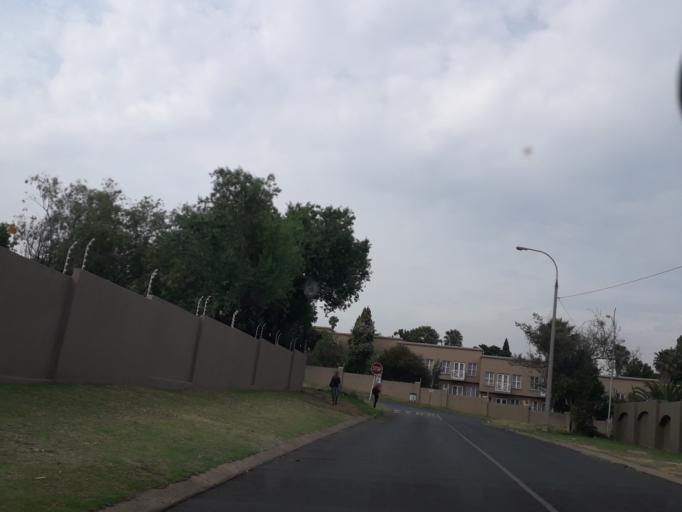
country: ZA
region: Gauteng
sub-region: City of Johannesburg Metropolitan Municipality
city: Roodepoort
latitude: -26.1022
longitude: 27.9216
